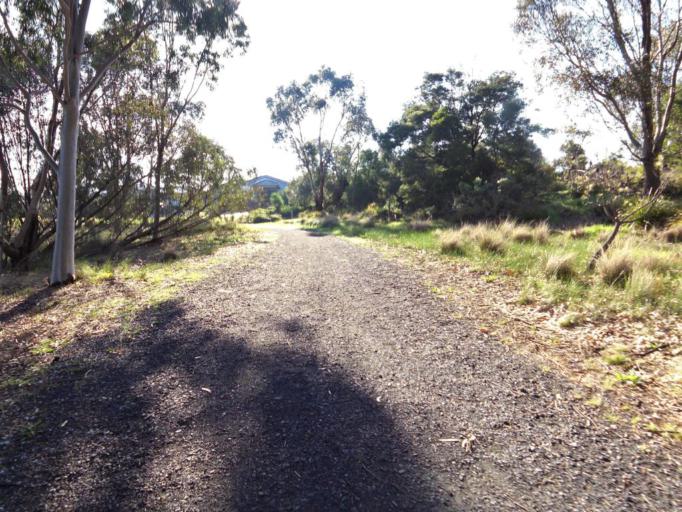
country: AU
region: Victoria
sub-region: Kingston
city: Waterways
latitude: -38.0196
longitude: 145.1379
